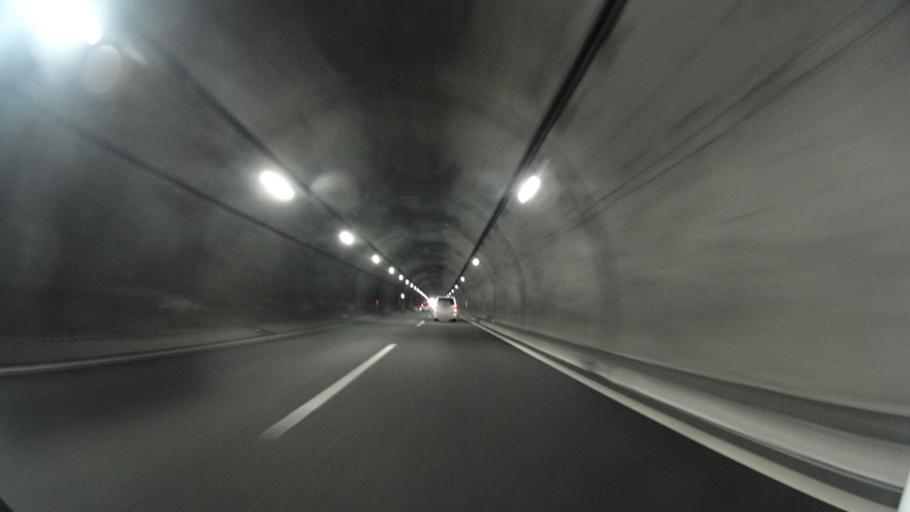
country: JP
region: Ehime
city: Saijo
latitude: 33.8862
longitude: 133.1593
